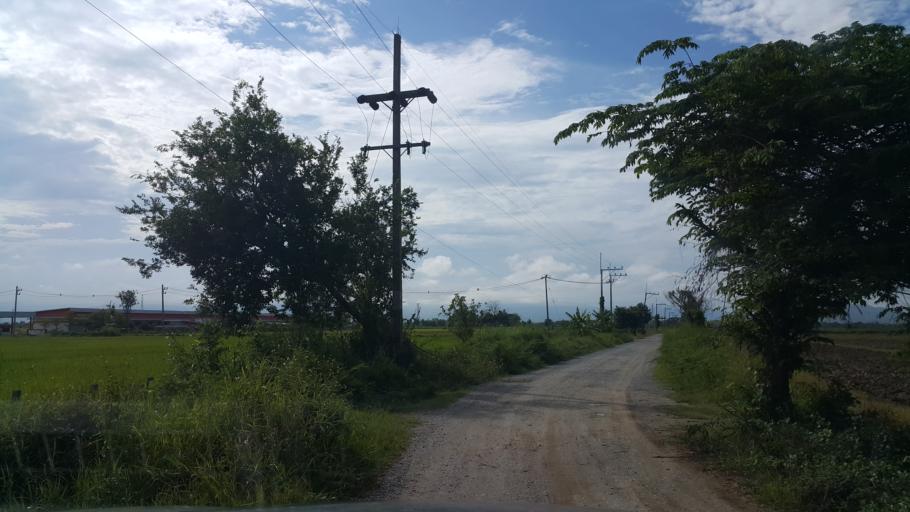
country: TH
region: Chiang Rai
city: Wiang Chai
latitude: 19.9529
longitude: 99.9301
